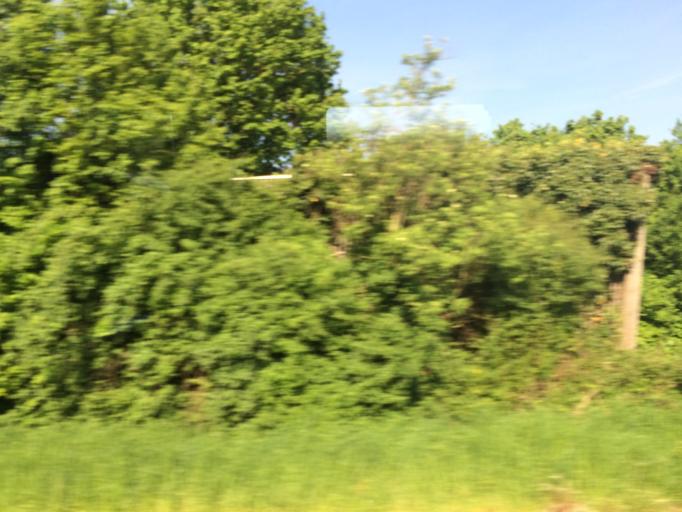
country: DE
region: North Rhine-Westphalia
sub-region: Regierungsbezirk Dusseldorf
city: Langenfeld
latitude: 51.1135
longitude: 6.9280
